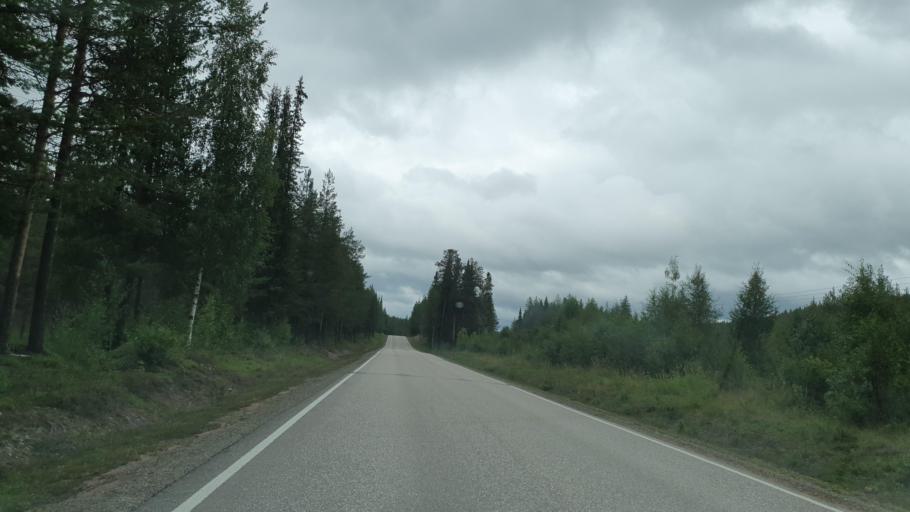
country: FI
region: Lapland
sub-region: Tunturi-Lappi
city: Kolari
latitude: 67.5559
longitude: 24.0096
